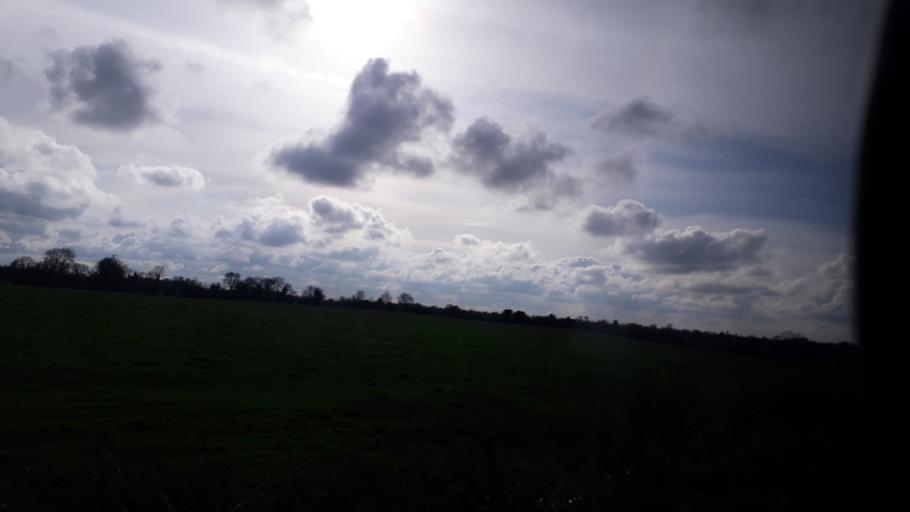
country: IE
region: Leinster
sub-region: An Mhi
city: Longwood
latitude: 53.4438
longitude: -6.9366
